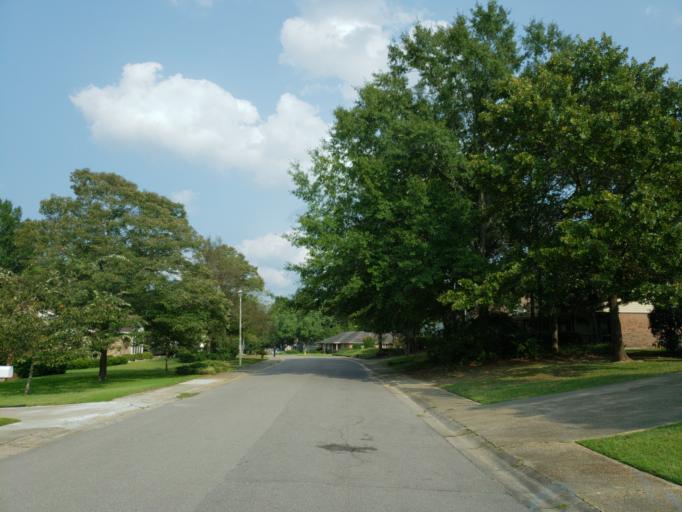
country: US
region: Mississippi
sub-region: Lamar County
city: West Hattiesburg
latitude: 31.3163
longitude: -89.3502
